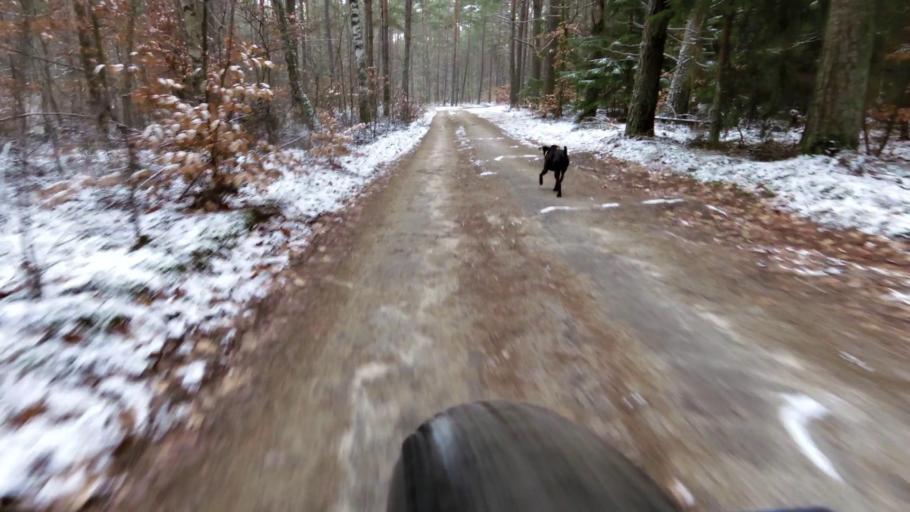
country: PL
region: West Pomeranian Voivodeship
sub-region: Powiat walecki
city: Miroslawiec
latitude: 53.3060
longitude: 16.0668
